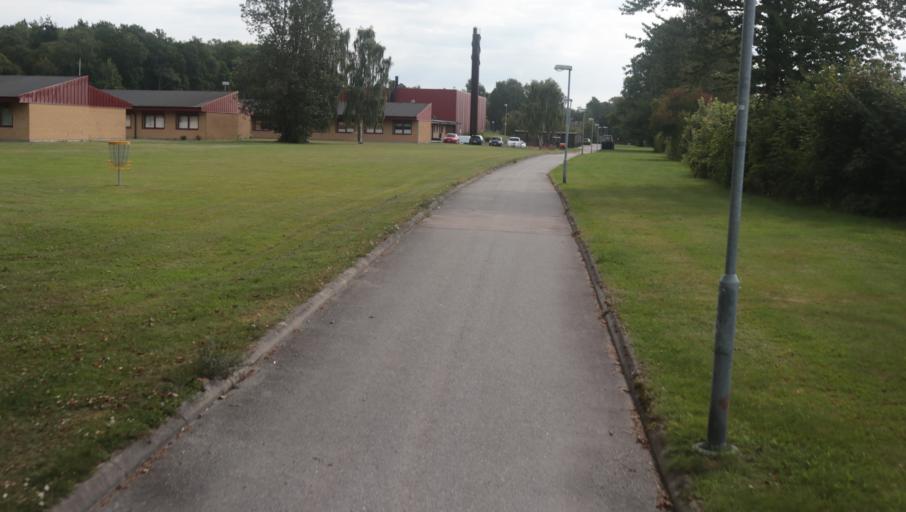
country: SE
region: Blekinge
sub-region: Karlshamns Kommun
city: Morrum
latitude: 56.2005
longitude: 14.7521
